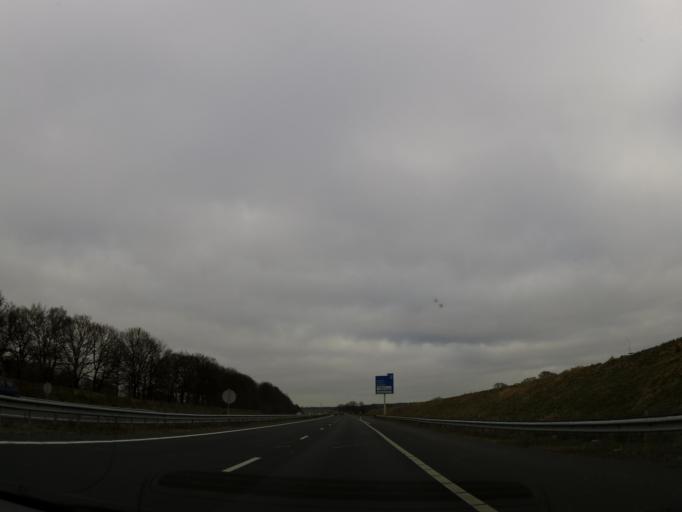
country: NL
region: Limburg
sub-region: Gemeente Venlo
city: Tegelen
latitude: 51.3101
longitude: 6.1269
